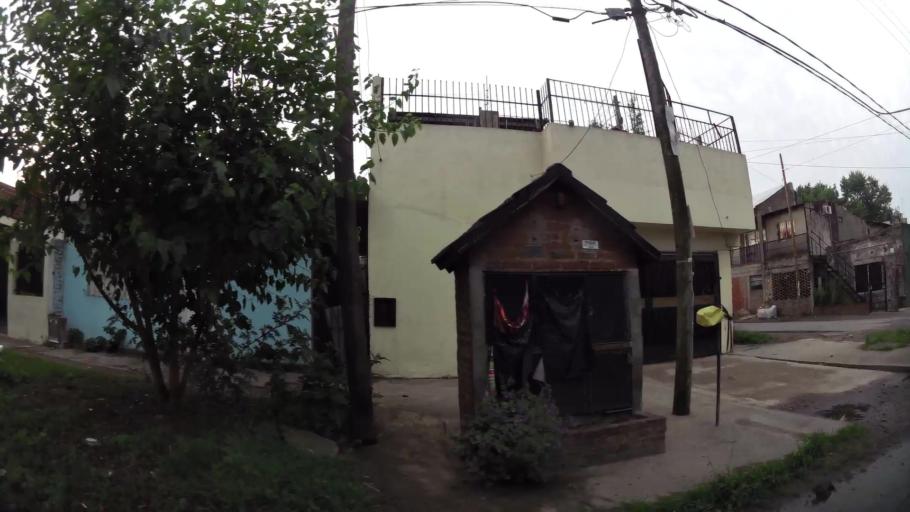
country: AR
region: Buenos Aires
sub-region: Partido de Lanus
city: Lanus
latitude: -34.7277
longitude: -58.3383
